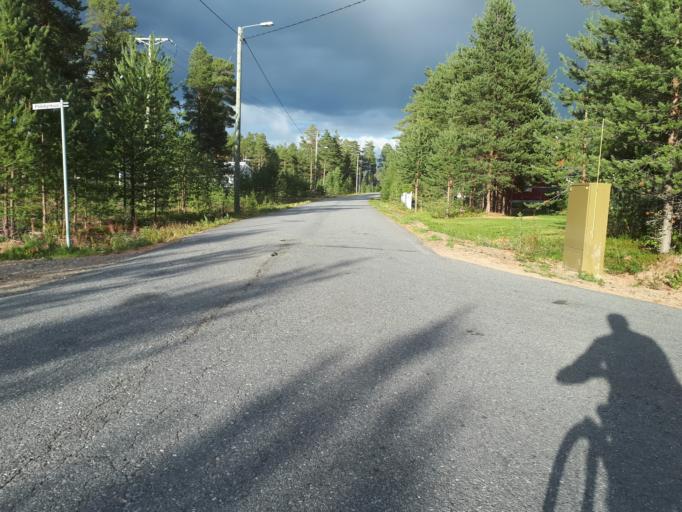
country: FI
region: Northern Ostrobothnia
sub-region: Oulunkaari
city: Ii
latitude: 65.3245
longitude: 25.4030
